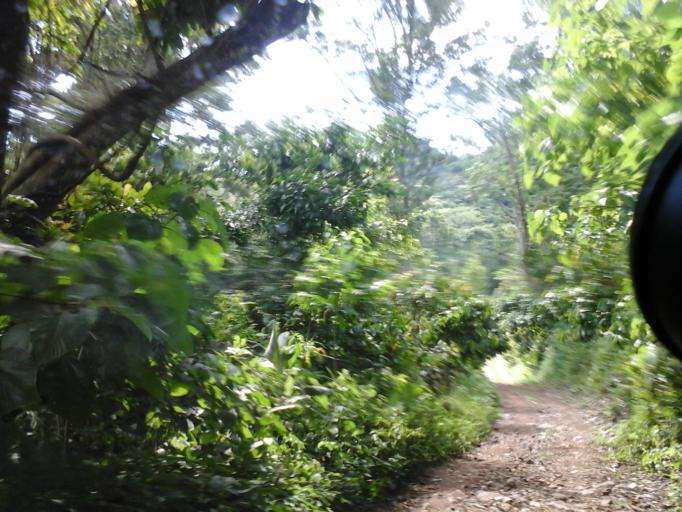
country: CO
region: Cesar
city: San Diego
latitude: 10.2752
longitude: -73.0927
